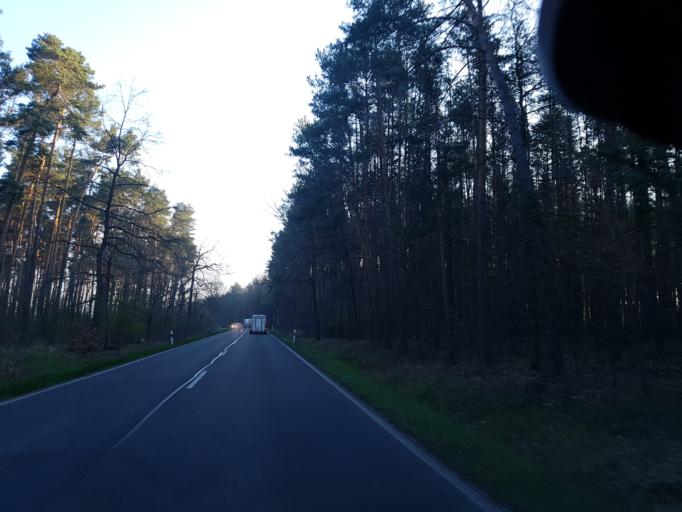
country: DE
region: Saxony-Anhalt
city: Holzdorf
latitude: 51.8490
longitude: 13.1466
